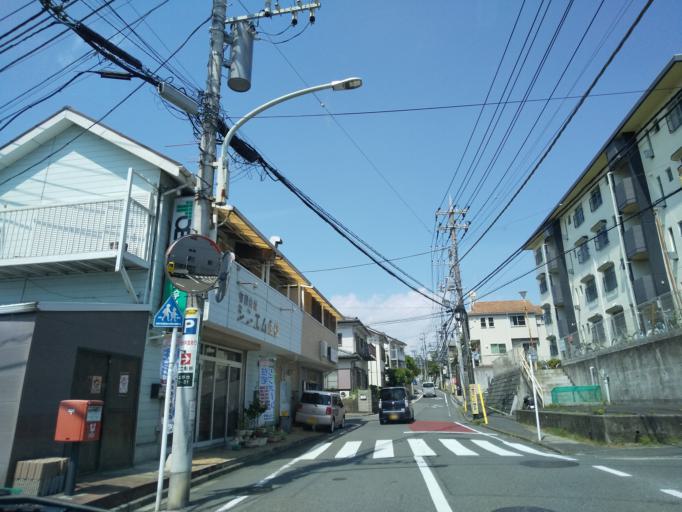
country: JP
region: Kanagawa
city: Zama
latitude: 35.5038
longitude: 139.4176
